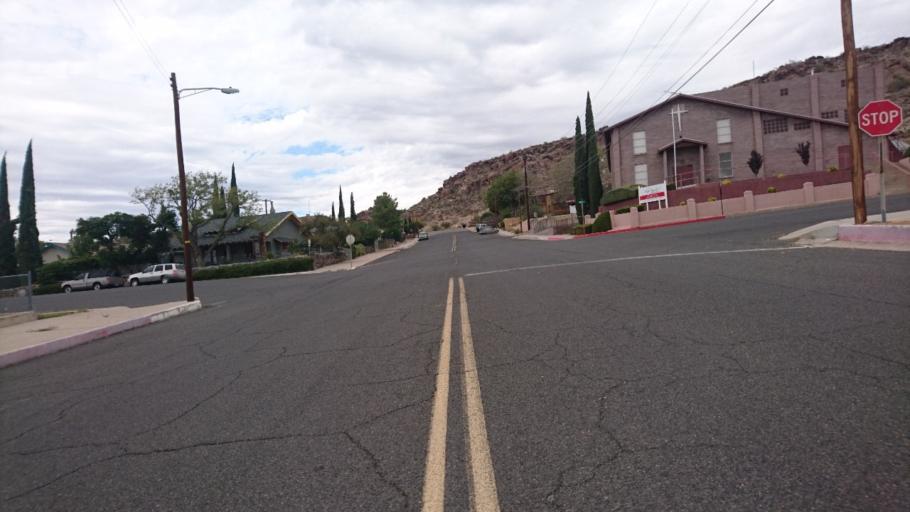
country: US
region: Arizona
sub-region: Mohave County
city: Kingman
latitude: 35.1899
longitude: -114.0492
